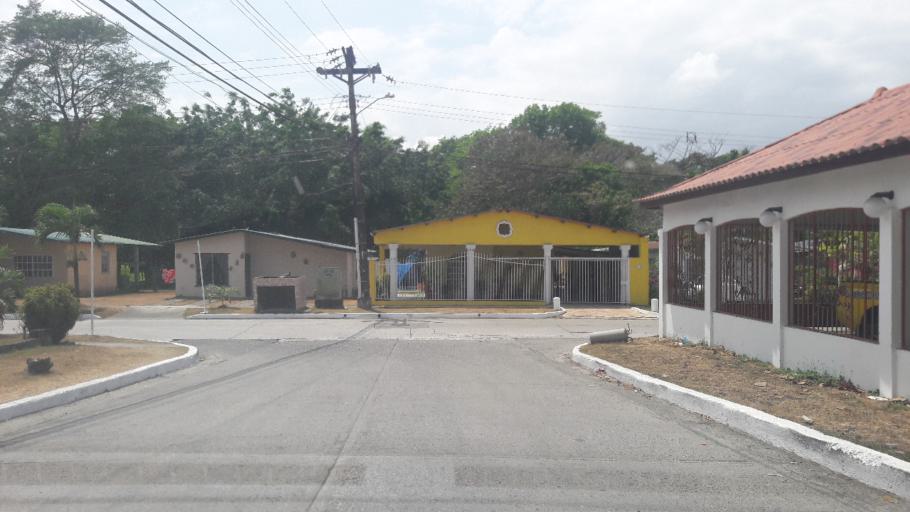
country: PA
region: Panama
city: Alcalde Diaz
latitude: 9.1397
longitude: -79.5530
